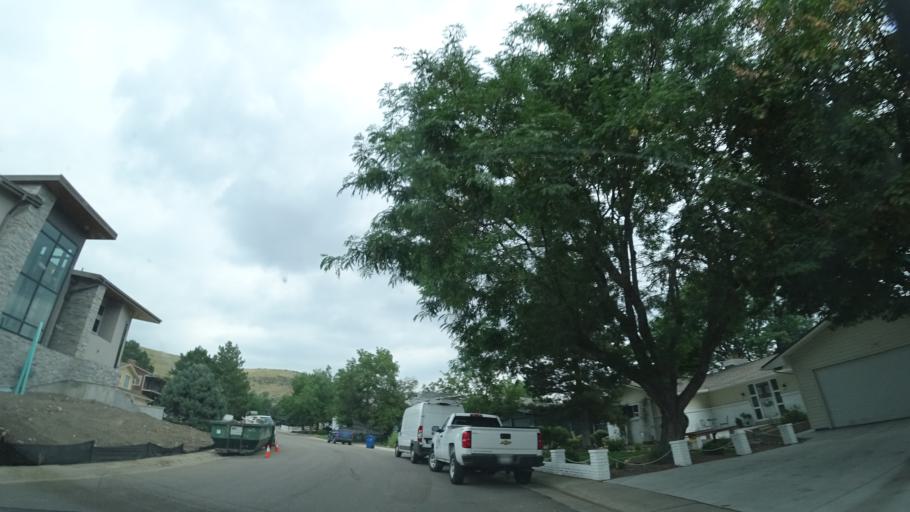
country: US
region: Colorado
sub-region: Jefferson County
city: West Pleasant View
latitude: 39.6964
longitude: -105.1511
